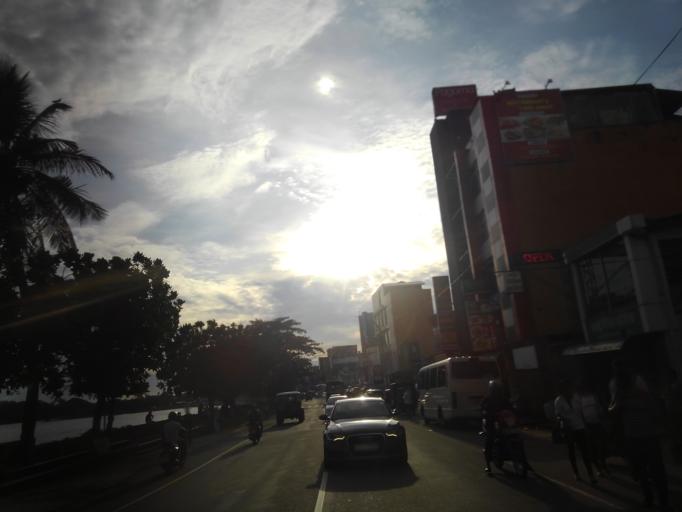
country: LK
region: Southern
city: Galle
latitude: 6.0358
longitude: 80.2211
